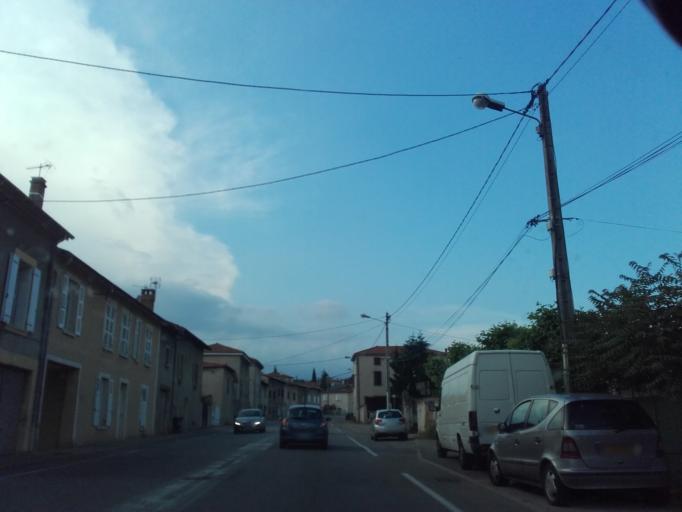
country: FR
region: Rhone-Alpes
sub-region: Departement de l'Isere
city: Le Peage-de-Roussillon
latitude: 45.3795
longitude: 4.7977
